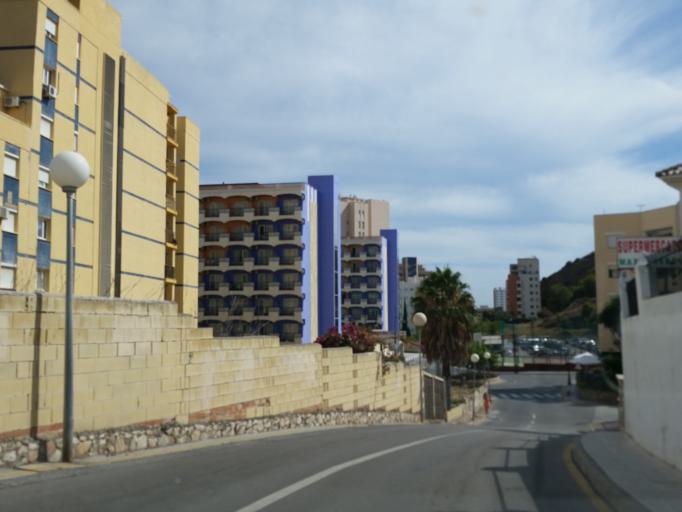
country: ES
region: Andalusia
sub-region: Provincia de Malaga
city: Fuengirola
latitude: 36.5640
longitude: -4.6072
